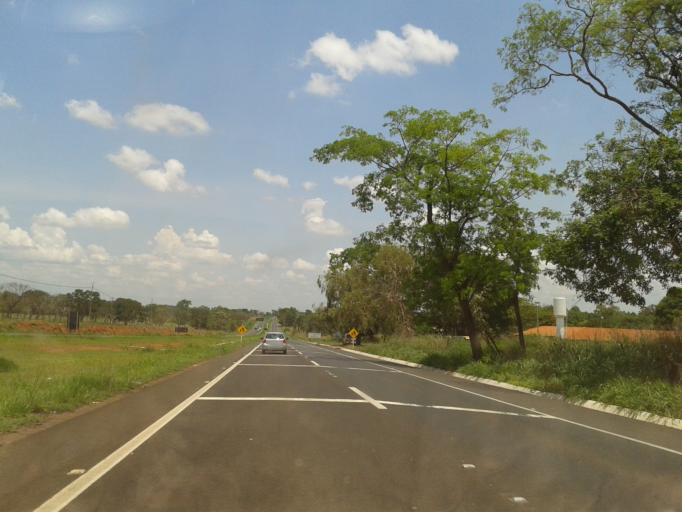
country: BR
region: Minas Gerais
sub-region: Monte Alegre De Minas
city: Monte Alegre de Minas
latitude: -18.8736
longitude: -48.6002
